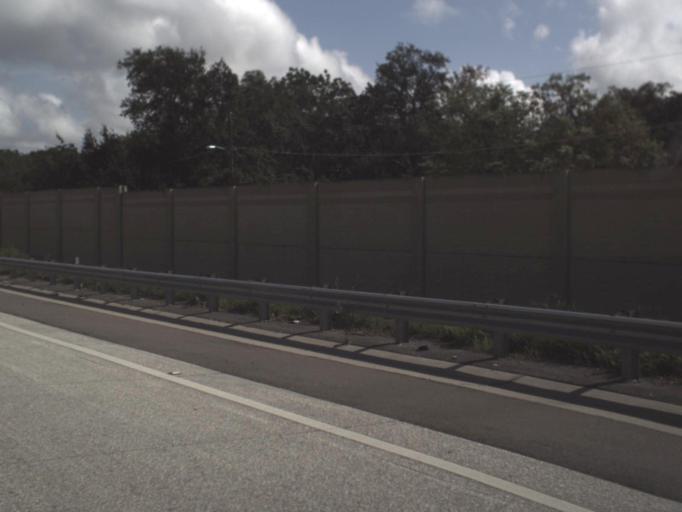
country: US
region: Florida
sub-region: Hillsborough County
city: University
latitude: 28.0461
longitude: -82.4548
